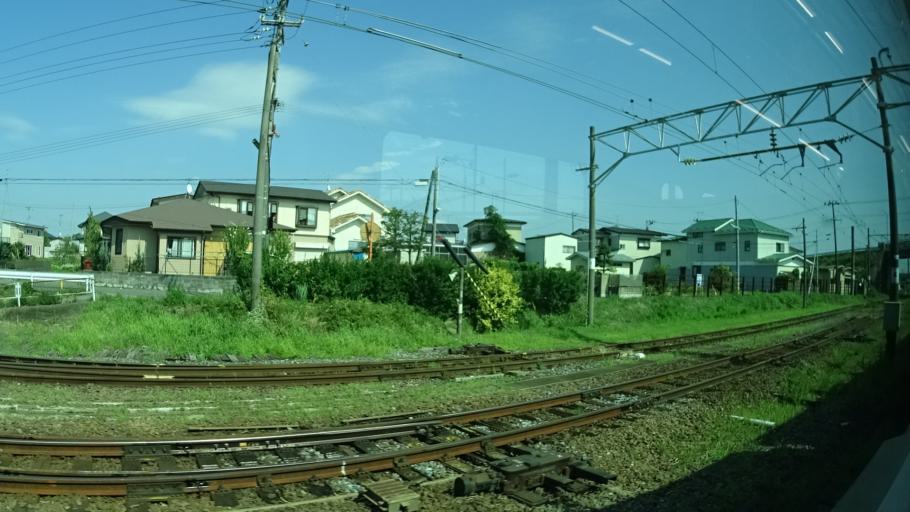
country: JP
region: Miyagi
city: Kogota
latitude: 38.5348
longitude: 141.0649
